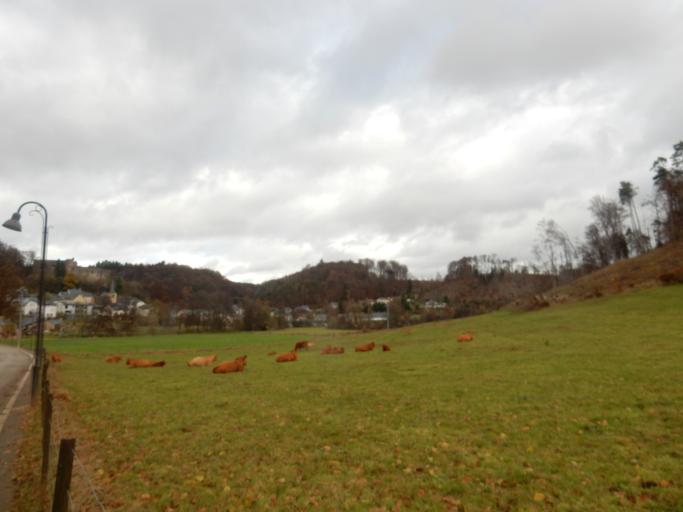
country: LU
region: Luxembourg
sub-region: Canton de Capellen
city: Septfontaines
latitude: 49.6957
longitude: 5.9656
